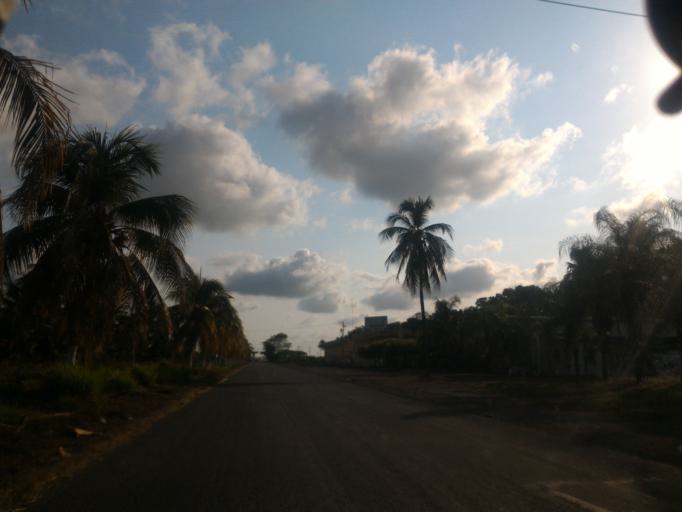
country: MX
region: Colima
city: Tecoman
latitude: 18.9014
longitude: -103.8577
